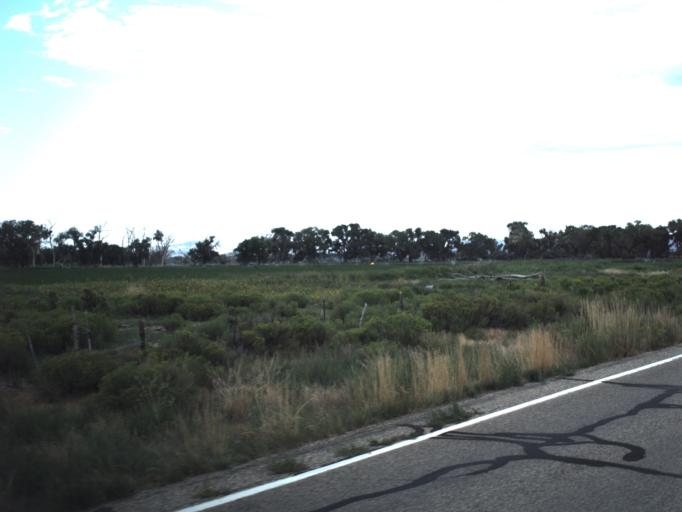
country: US
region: Utah
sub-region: Emery County
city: Huntington
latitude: 39.4292
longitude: -110.8624
